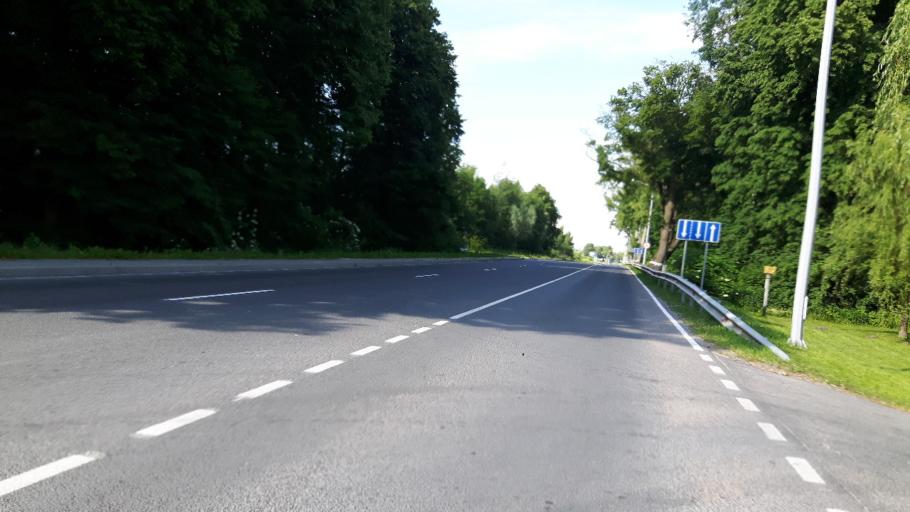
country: RU
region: Kaliningrad
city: Mamonovo
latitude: 54.4470
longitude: 19.9132
